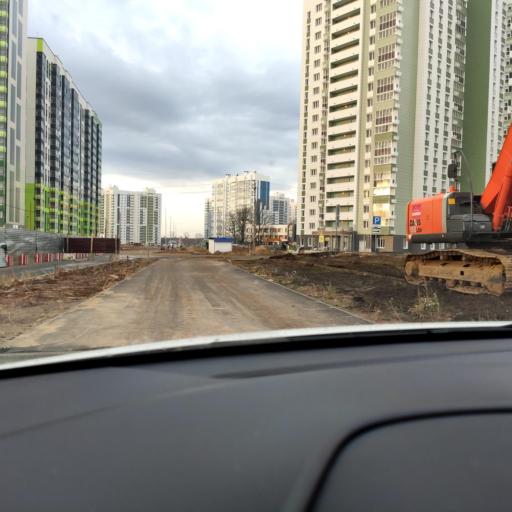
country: RU
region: Tatarstan
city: Osinovo
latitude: 55.8588
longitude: 48.9044
